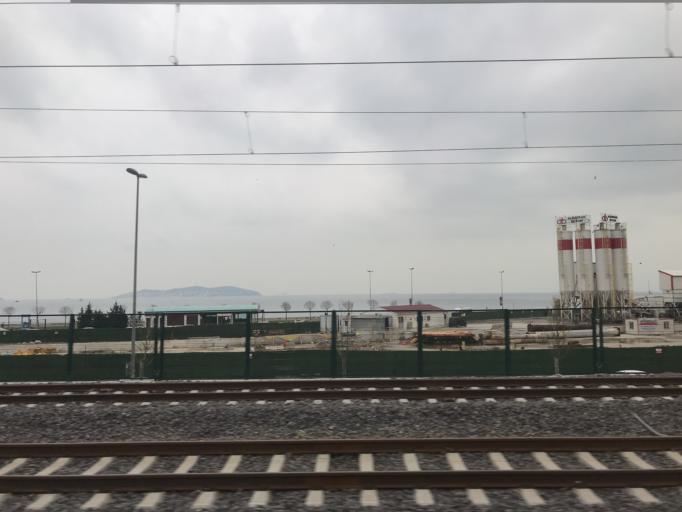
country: TR
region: Istanbul
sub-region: Atasehir
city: Atasehir
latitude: 40.9506
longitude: 29.0996
